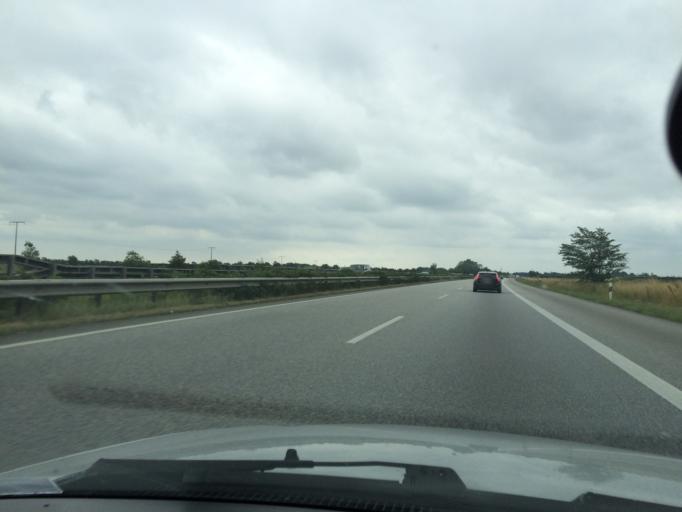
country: DE
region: Schleswig-Holstein
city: Sankelmark
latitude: 54.7190
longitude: 9.3988
